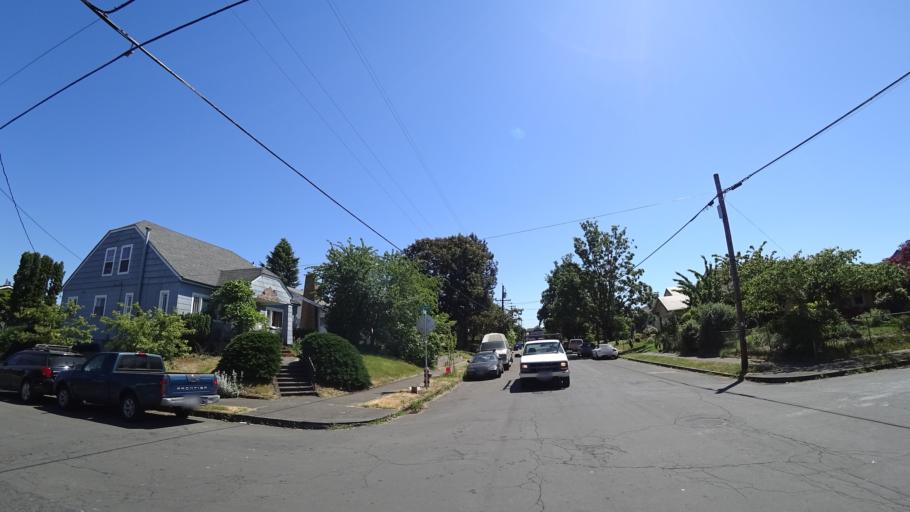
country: US
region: Oregon
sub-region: Multnomah County
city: Portland
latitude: 45.5677
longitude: -122.6594
